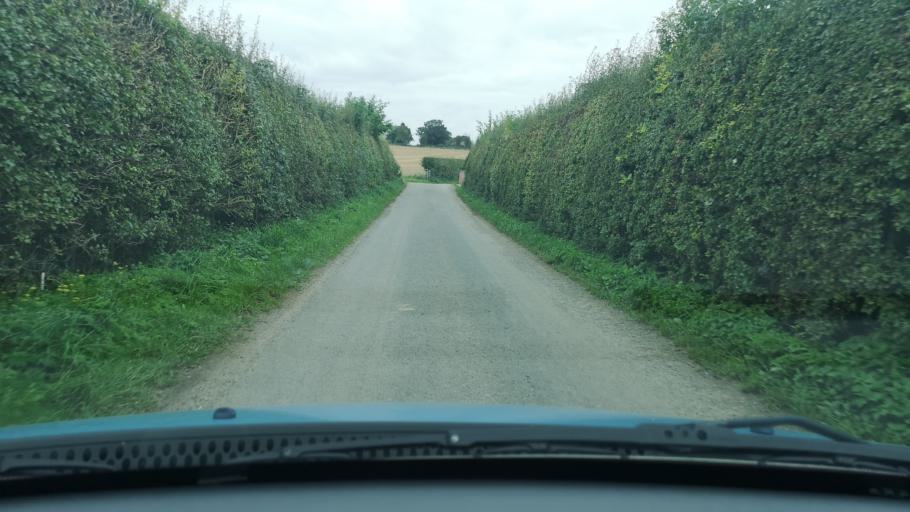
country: GB
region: England
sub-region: City and Borough of Wakefield
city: Featherstone
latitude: 53.6589
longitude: -1.3642
